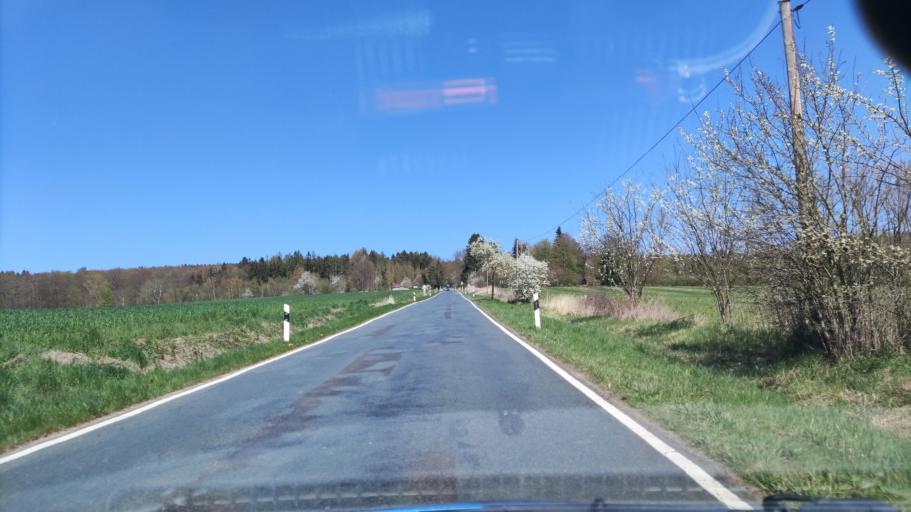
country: DE
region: Lower Saxony
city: Eimen
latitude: 51.8796
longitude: 9.8040
